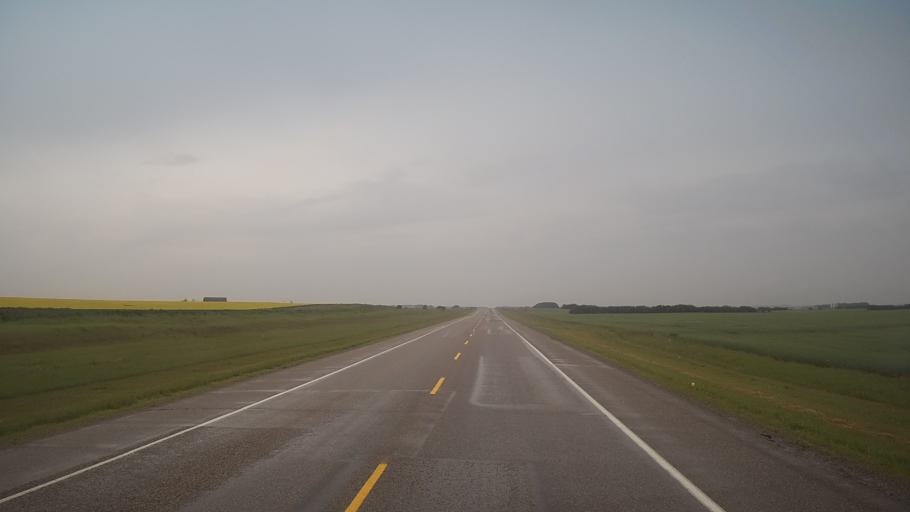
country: CA
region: Saskatchewan
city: Wilkie
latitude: 52.2213
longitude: -108.5172
